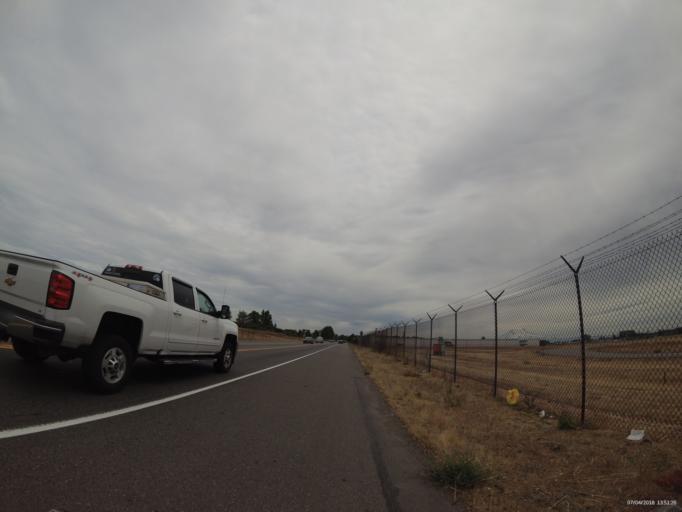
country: US
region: Washington
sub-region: Pierce County
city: McChord Air Force Base
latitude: 47.1558
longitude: -122.4763
